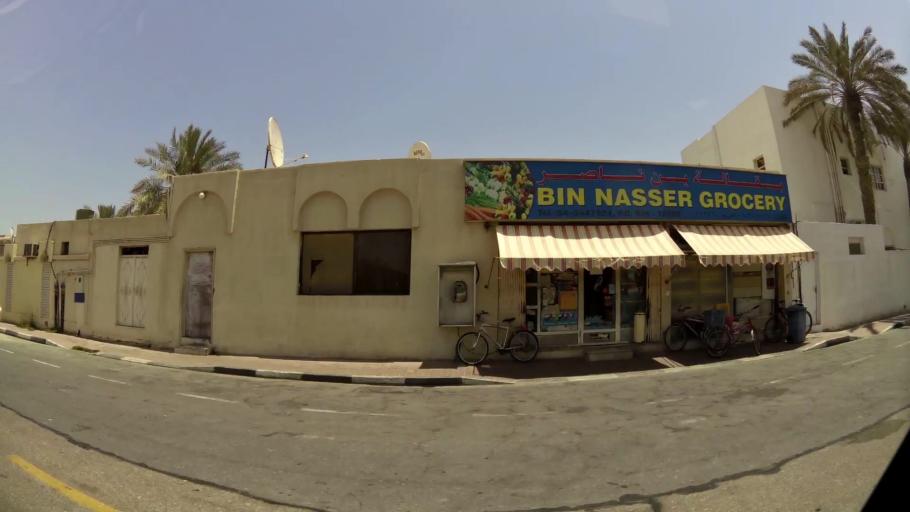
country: AE
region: Dubai
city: Dubai
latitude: 25.1946
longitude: 55.2508
